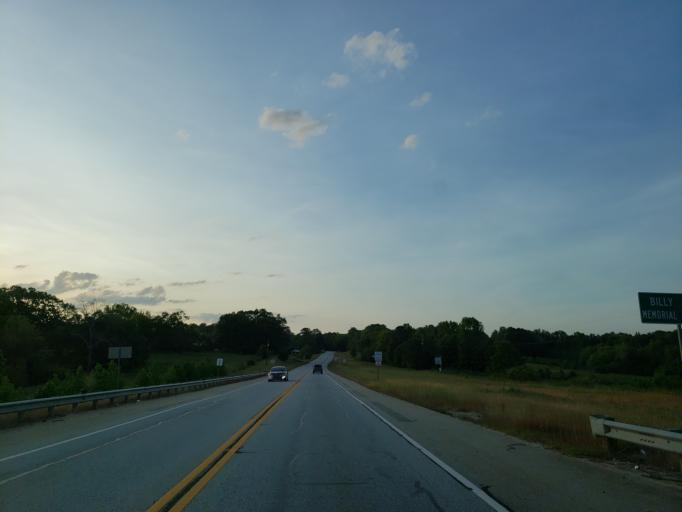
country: US
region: Georgia
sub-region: Coweta County
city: Newnan
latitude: 33.4777
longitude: -84.9018
